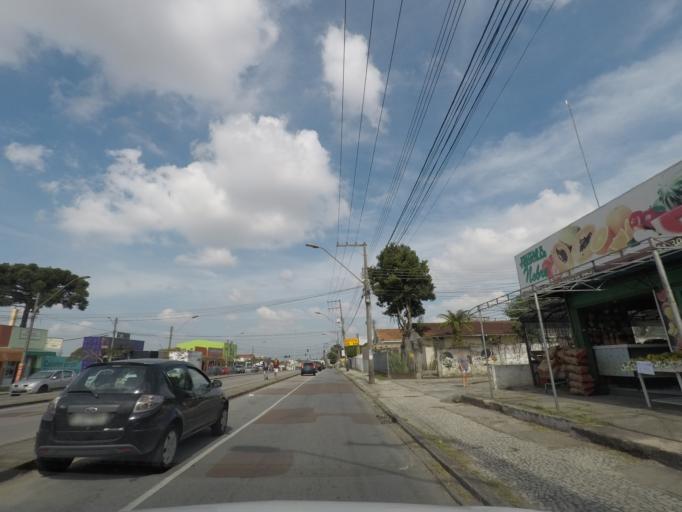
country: BR
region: Parana
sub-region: Pinhais
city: Pinhais
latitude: -25.4531
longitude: -49.2146
